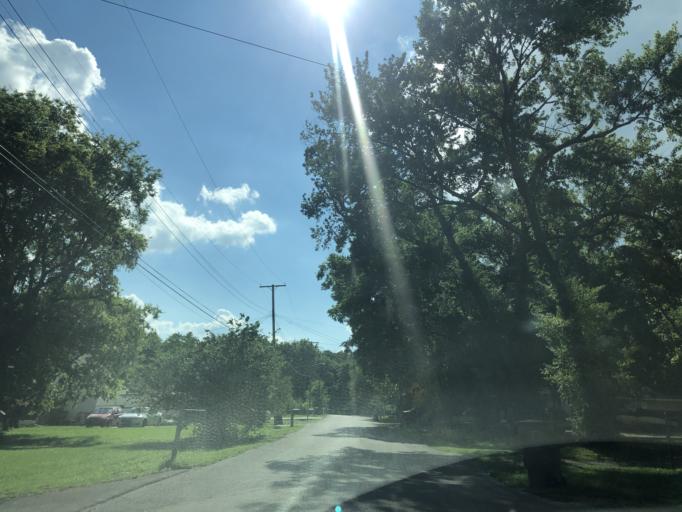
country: US
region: Tennessee
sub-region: Davidson County
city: Nashville
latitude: 36.2160
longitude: -86.7613
